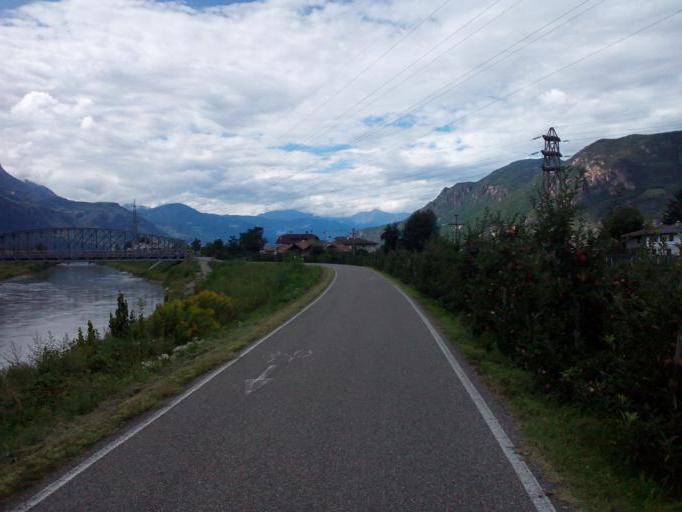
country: IT
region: Trentino-Alto Adige
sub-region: Bolzano
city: Cornaiano
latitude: 46.4820
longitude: 11.3068
